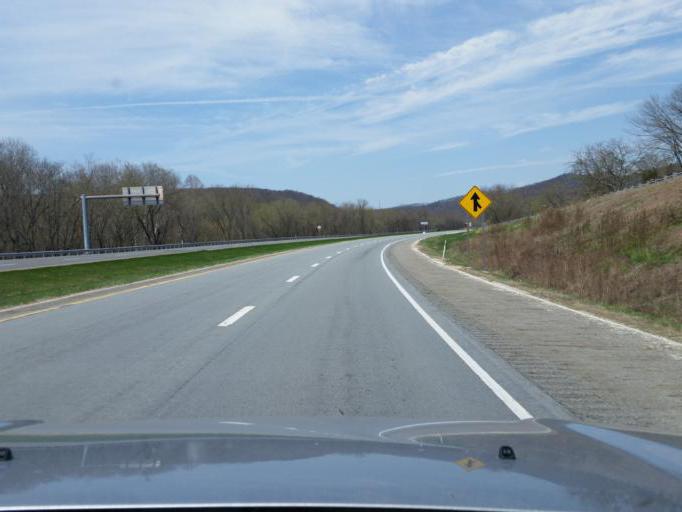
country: US
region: Pennsylvania
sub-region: Perry County
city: Newport
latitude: 40.5448
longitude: -77.1525
